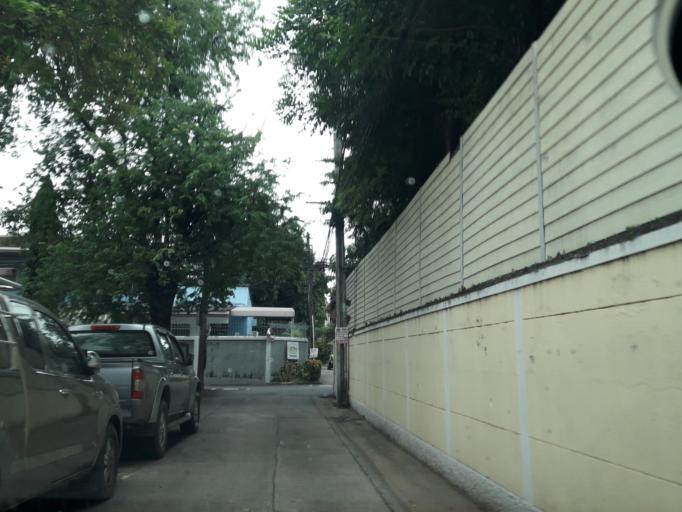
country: TH
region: Bangkok
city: Khlong Toei
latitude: 13.7364
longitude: 100.5544
